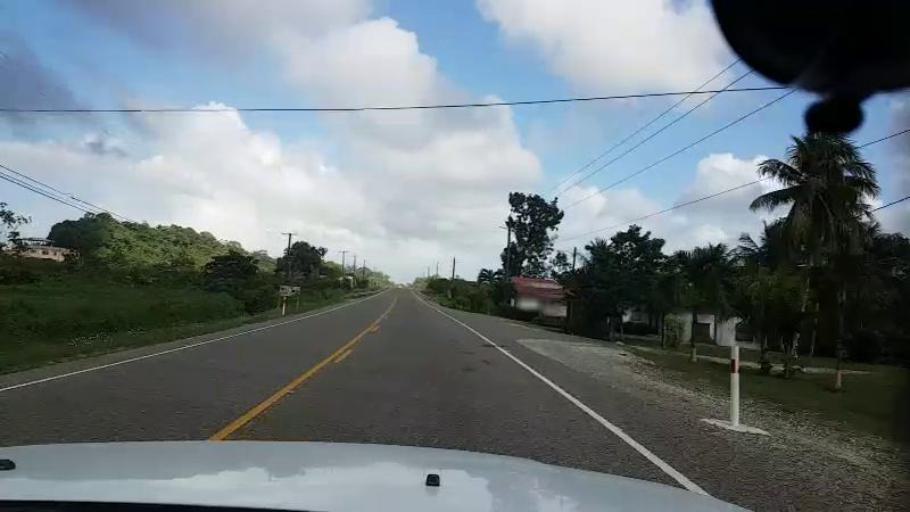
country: BZ
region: Stann Creek
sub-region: Dangriga
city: Dangriga
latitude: 16.9943
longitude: -88.3616
